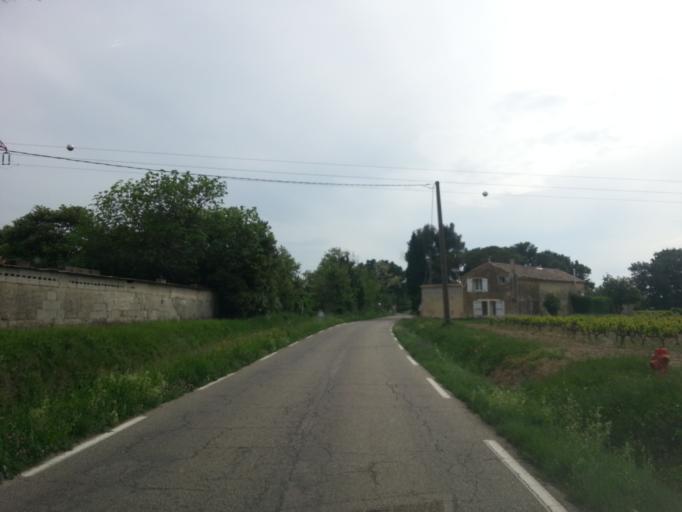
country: FR
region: Provence-Alpes-Cote d'Azur
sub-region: Departement du Vaucluse
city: Camaret-sur-Aigues
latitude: 44.1721
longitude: 4.8861
